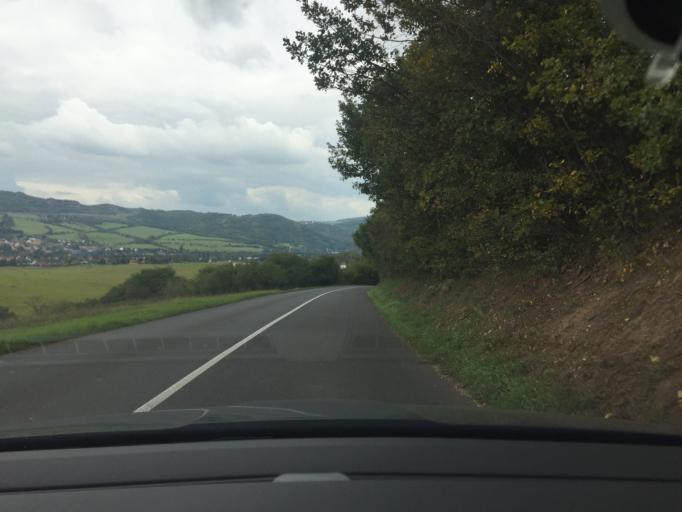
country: CZ
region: Ustecky
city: Lovosice
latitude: 50.5609
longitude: 14.0622
